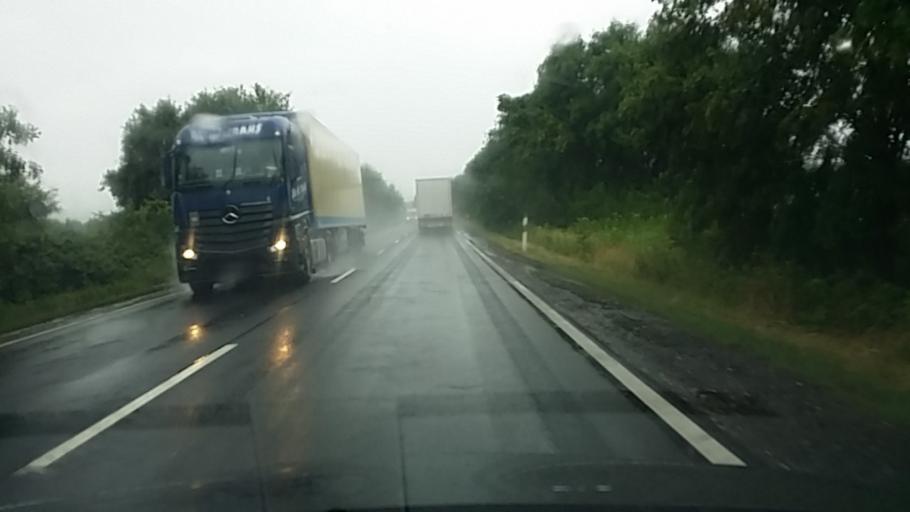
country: HU
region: Nograd
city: Retsag
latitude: 47.9672
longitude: 19.1285
